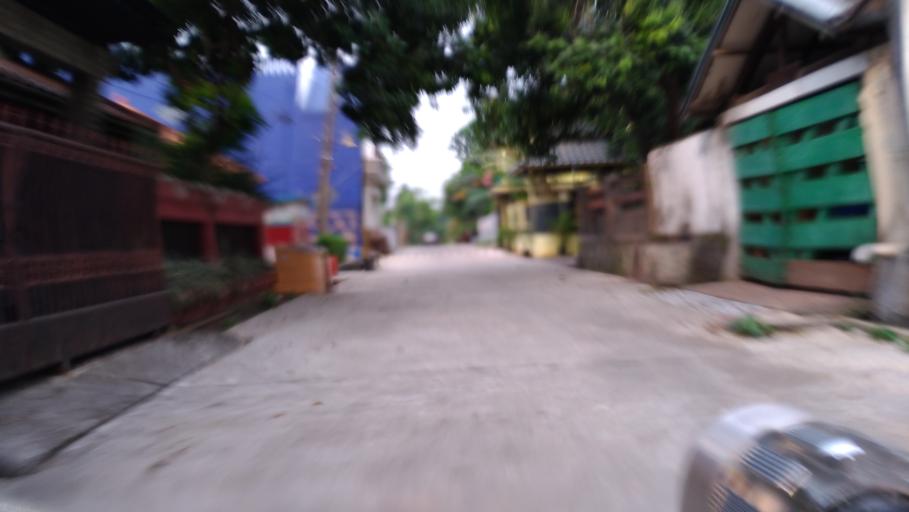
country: ID
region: West Java
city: Depok
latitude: -6.3635
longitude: 106.8622
